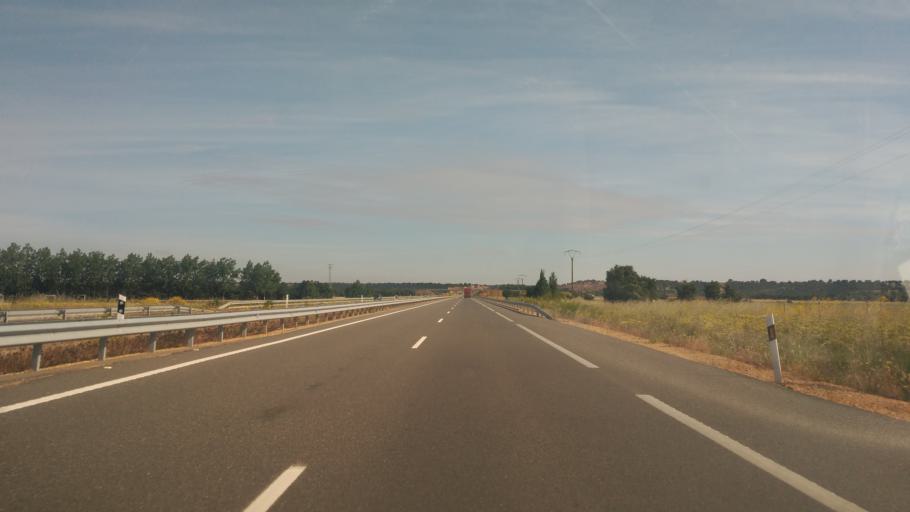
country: ES
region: Castille and Leon
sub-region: Provincia de Salamanca
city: Topas
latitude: 41.2012
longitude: -5.7001
